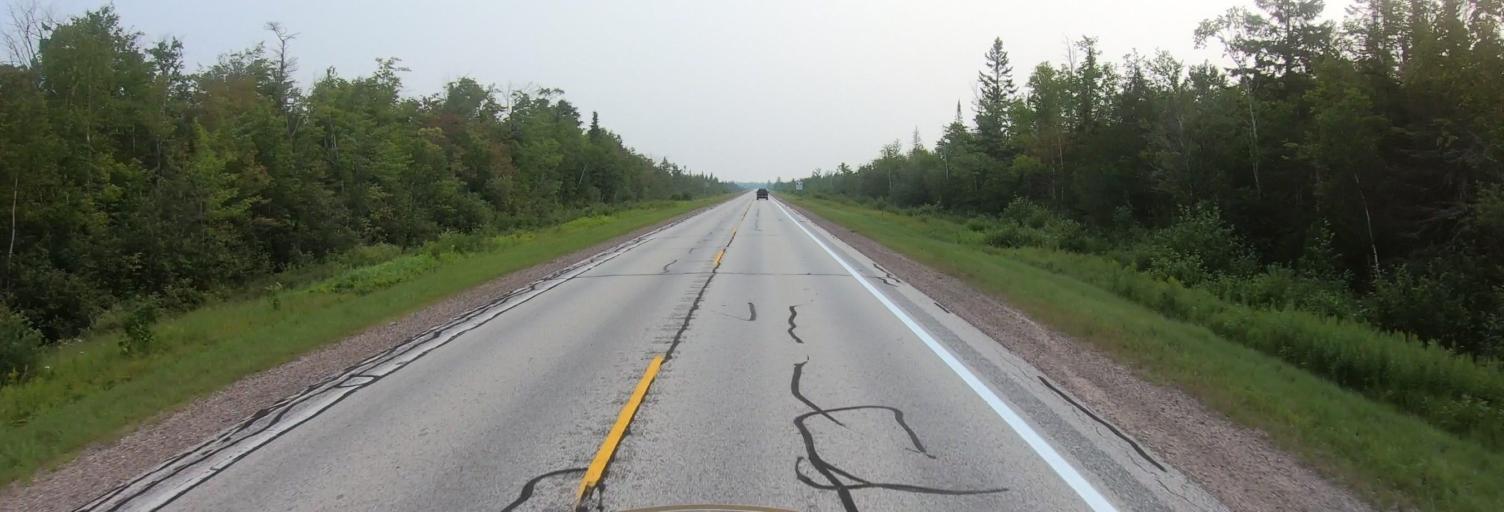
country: US
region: Michigan
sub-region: Luce County
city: Newberry
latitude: 46.5301
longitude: -85.0632
